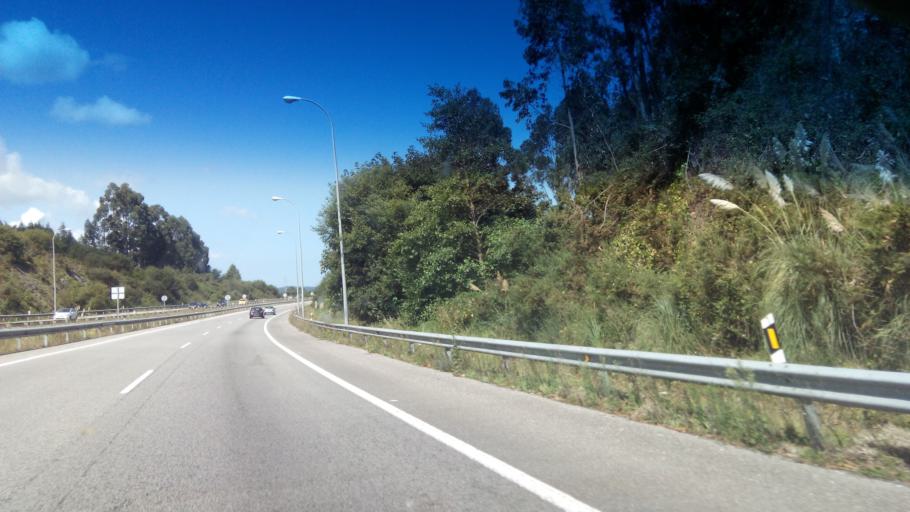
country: ES
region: Asturias
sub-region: Province of Asturias
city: Colunga
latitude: 43.4689
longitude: -5.2123
